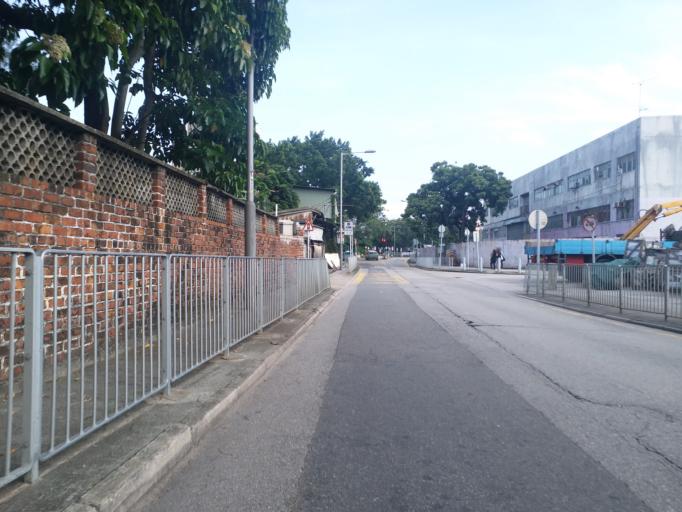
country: HK
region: Yuen Long
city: Yuen Long Kau Hui
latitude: 22.4434
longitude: 114.0107
